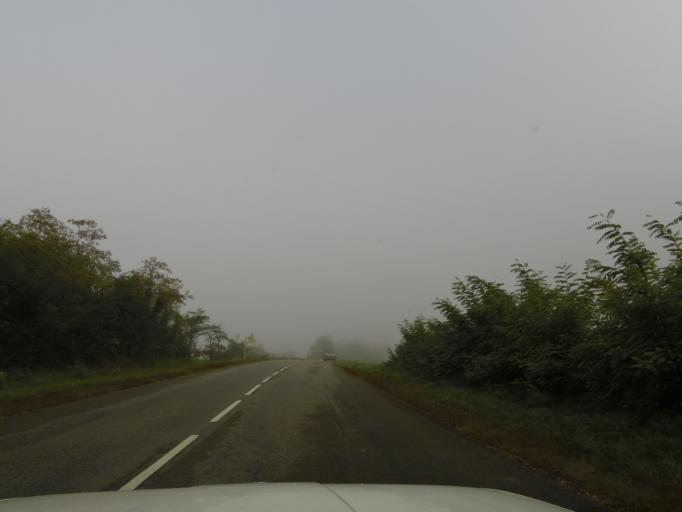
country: FR
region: Rhone-Alpes
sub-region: Departement de l'Isere
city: Creys-Mepieu
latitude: 45.7739
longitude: 5.4738
